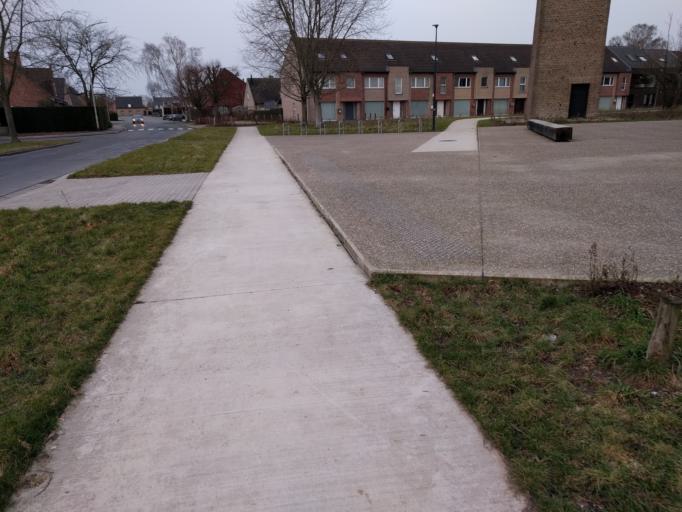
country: BE
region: Flanders
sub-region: Provincie West-Vlaanderen
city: Wevelgem
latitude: 50.8171
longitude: 3.1750
